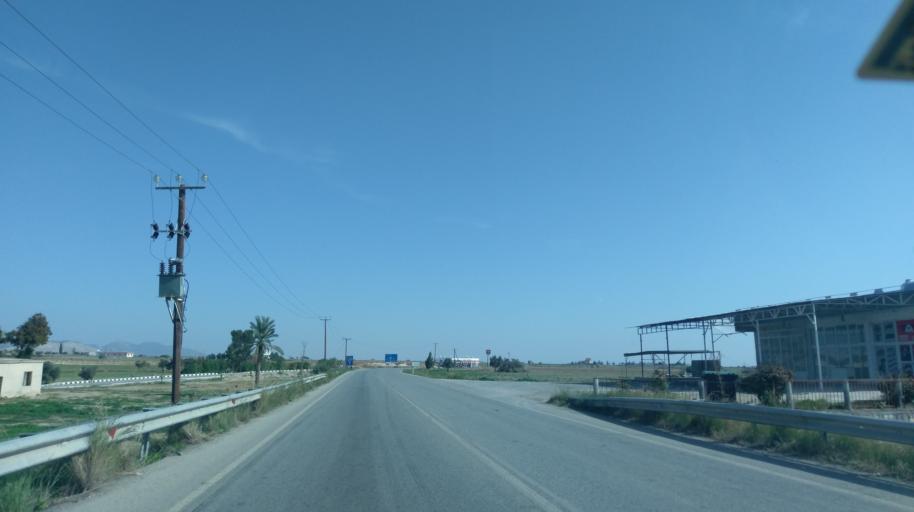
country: CY
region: Ammochostos
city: Lefkonoiko
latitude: 35.2600
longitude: 33.7414
